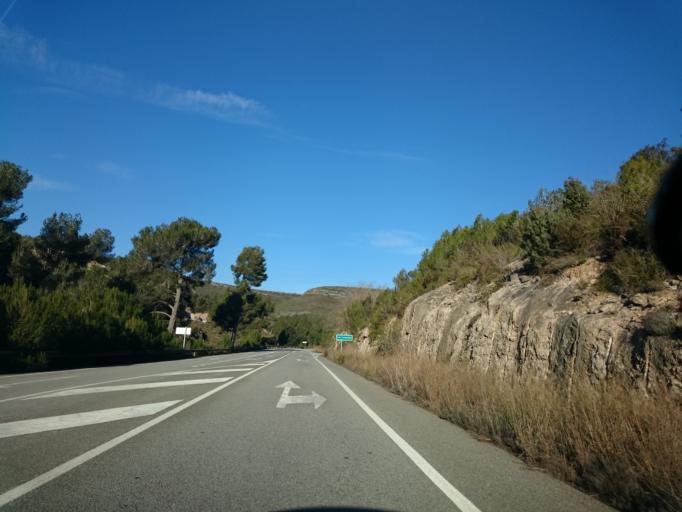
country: ES
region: Catalonia
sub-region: Provincia de Barcelona
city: Sant Pere de Ribes
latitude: 41.3014
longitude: 1.7273
